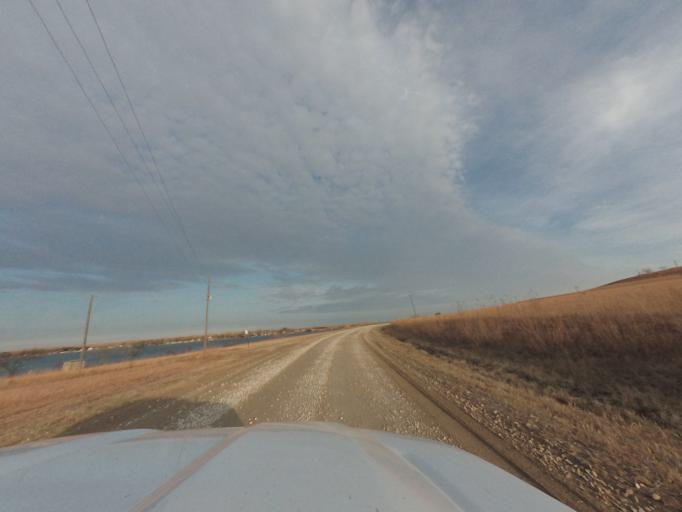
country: US
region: Kansas
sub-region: Morris County
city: Council Grove
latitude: 38.5203
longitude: -96.4115
